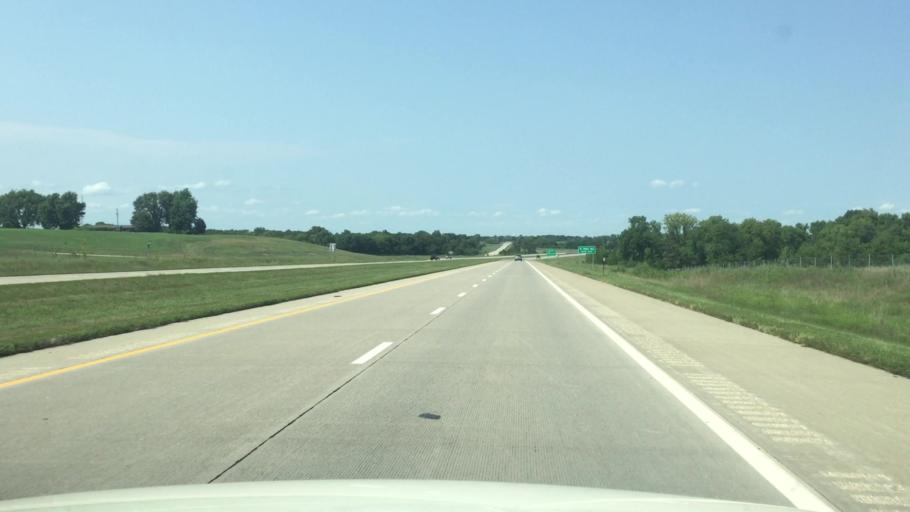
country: US
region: Kansas
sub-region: Linn County
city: Pleasanton
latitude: 38.1301
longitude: -94.7133
